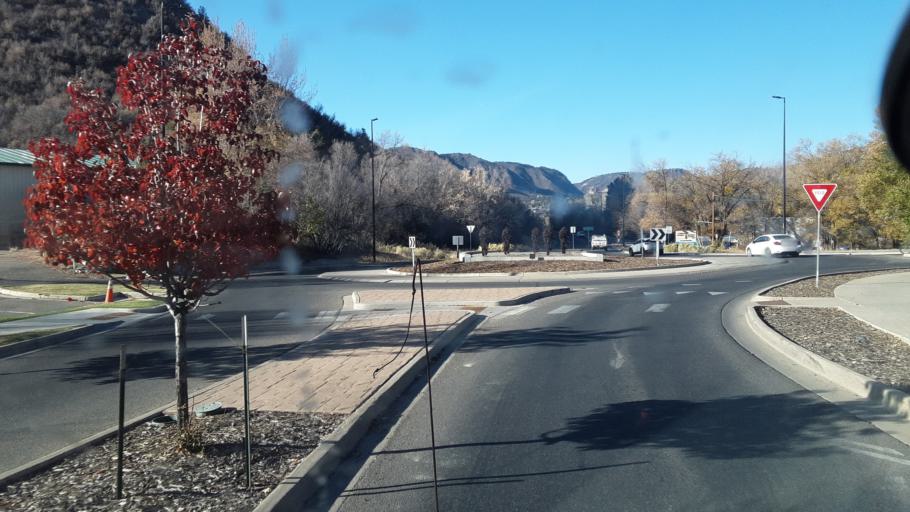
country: US
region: Colorado
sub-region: La Plata County
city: Durango
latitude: 37.2835
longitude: -107.8687
